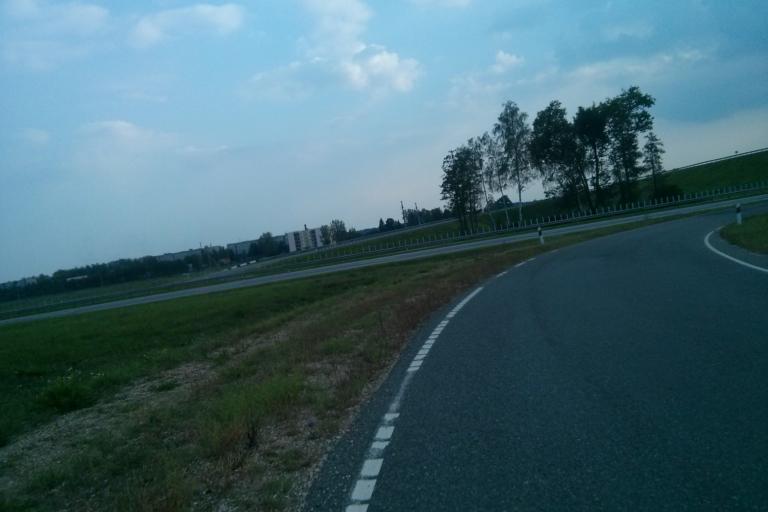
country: BY
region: Minsk
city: Chervyen'
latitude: 53.7250
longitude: 28.3958
